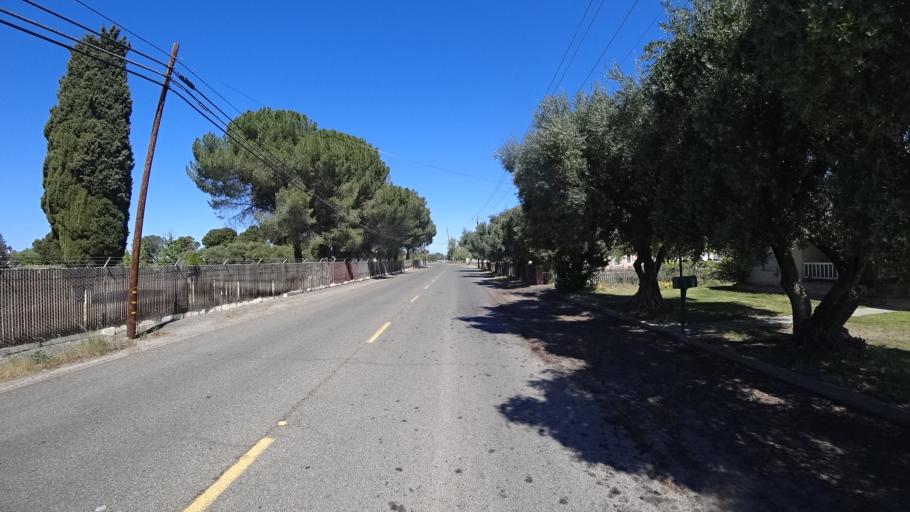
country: US
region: California
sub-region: Glenn County
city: Orland
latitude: 39.7423
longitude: -122.1780
